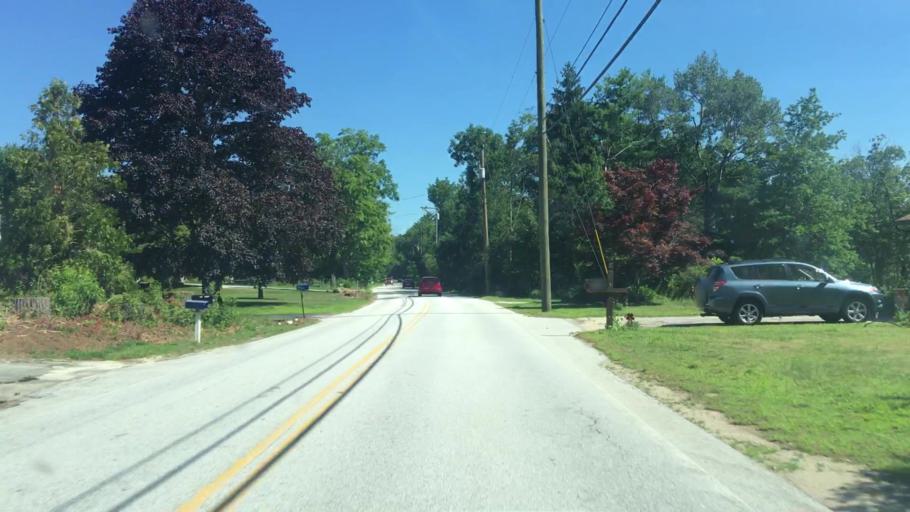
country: US
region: New Hampshire
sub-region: Rockingham County
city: Auburn
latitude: 43.0313
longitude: -71.3846
